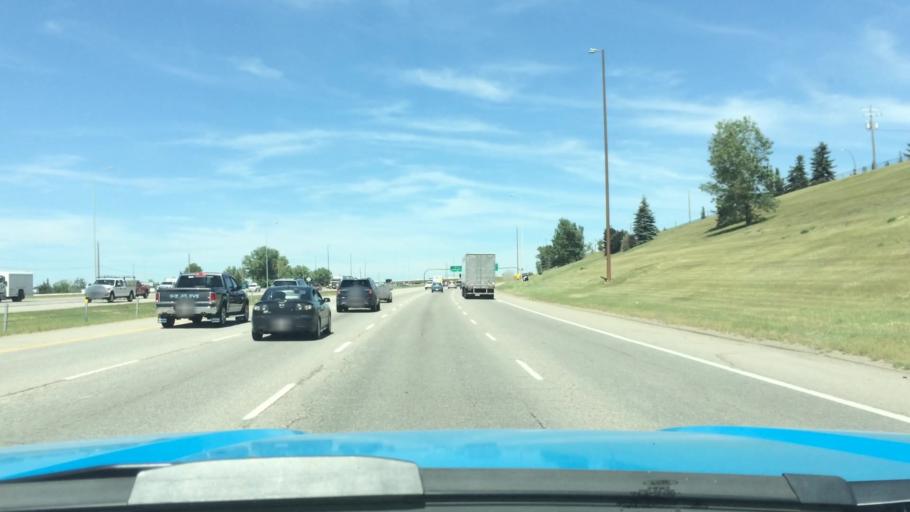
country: CA
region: Alberta
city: Calgary
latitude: 51.0885
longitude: -114.0387
